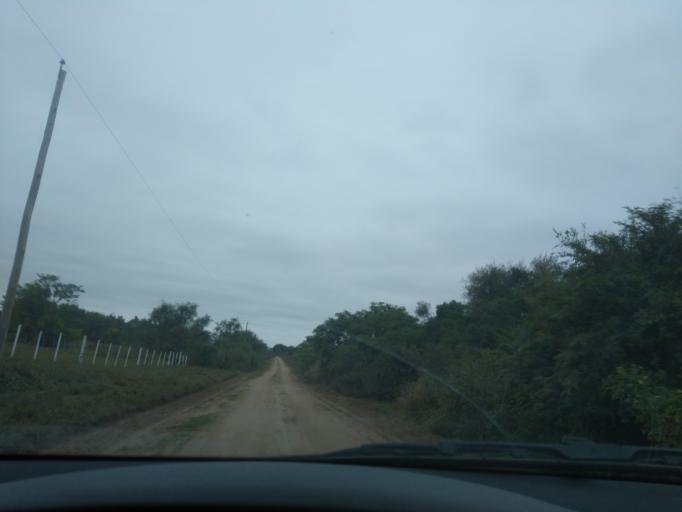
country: AR
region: Chaco
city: Colonia Benitez
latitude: -27.3701
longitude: -58.9486
